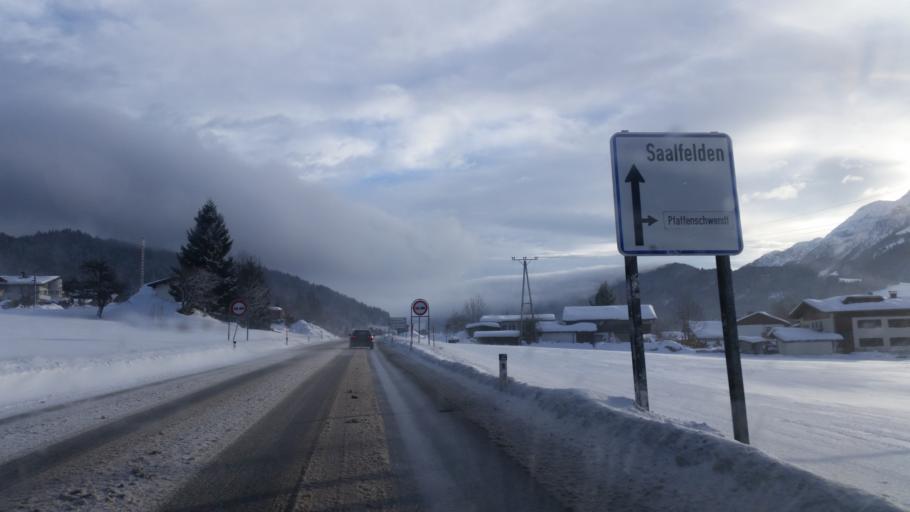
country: AT
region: Tyrol
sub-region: Politischer Bezirk Kitzbuhel
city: Fieberbrunn
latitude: 47.4681
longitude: 12.5770
